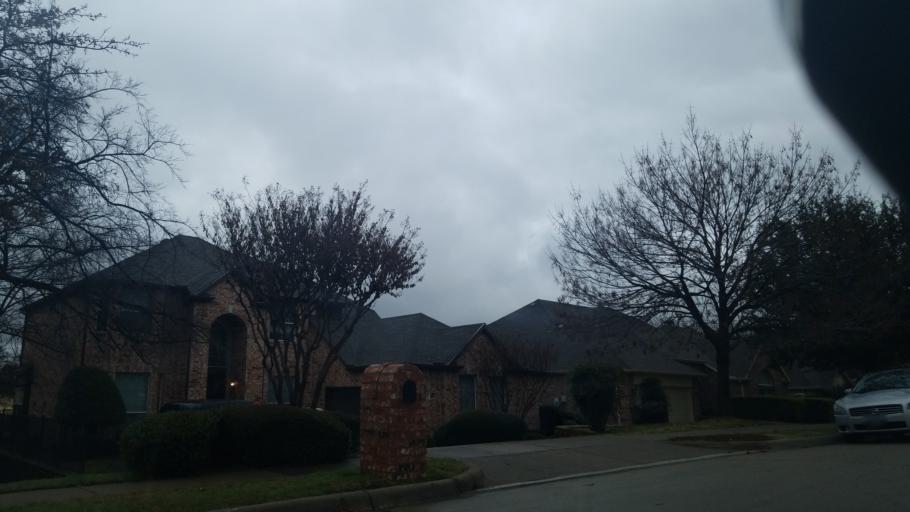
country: US
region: Texas
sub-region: Denton County
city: Corinth
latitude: 33.1464
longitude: -97.0889
